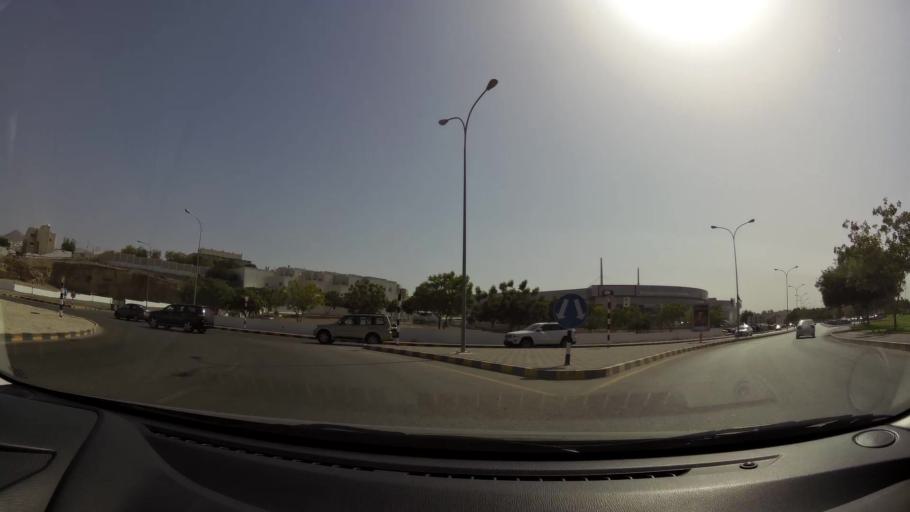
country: OM
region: Muhafazat Masqat
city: Muscat
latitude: 23.6094
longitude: 58.4962
